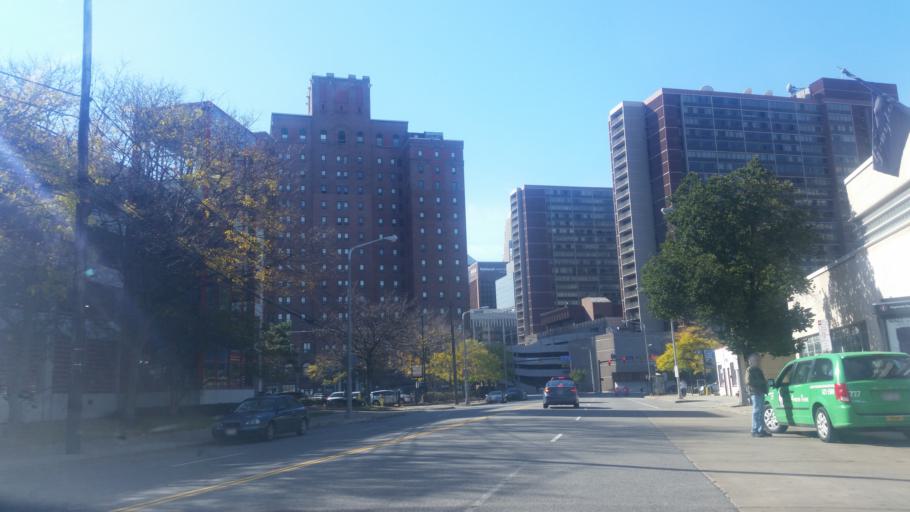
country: US
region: Ohio
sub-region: Cuyahoga County
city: Cleveland
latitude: 41.5031
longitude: -81.6820
